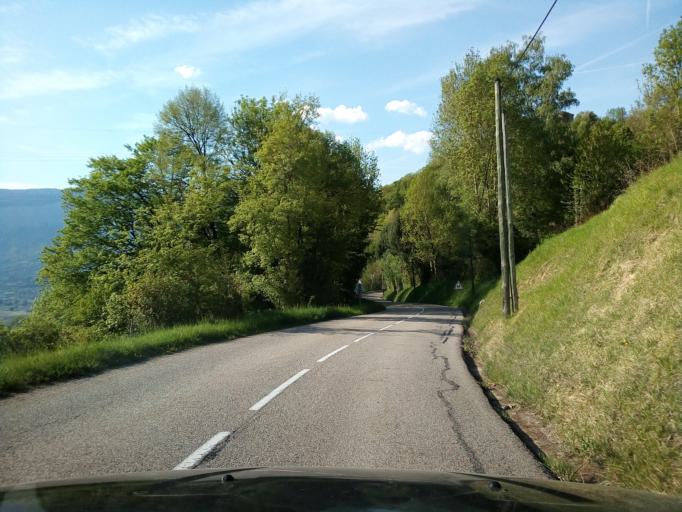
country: FR
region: Rhone-Alpes
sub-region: Departement de l'Isere
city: Revel
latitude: 45.1920
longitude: 5.8537
